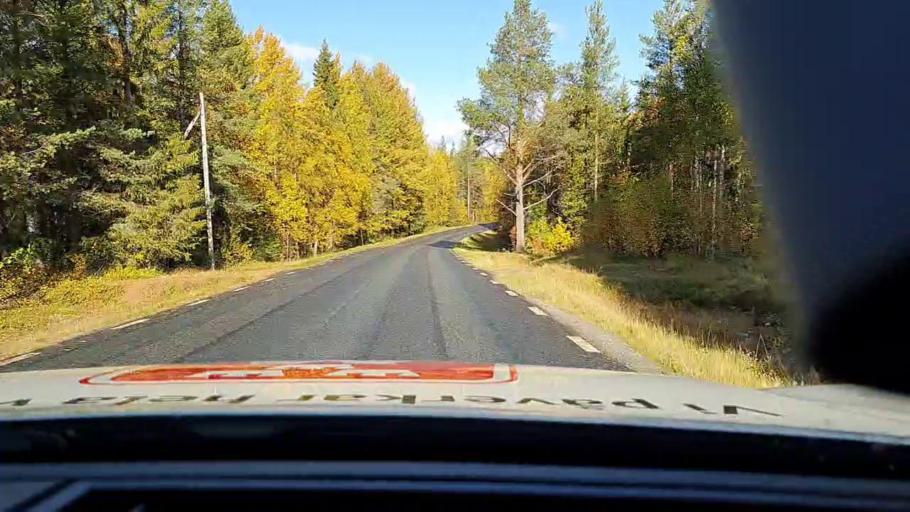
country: SE
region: Vaesterbotten
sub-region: Skelleftea Kommun
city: Langsele
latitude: 64.9999
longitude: 20.0906
